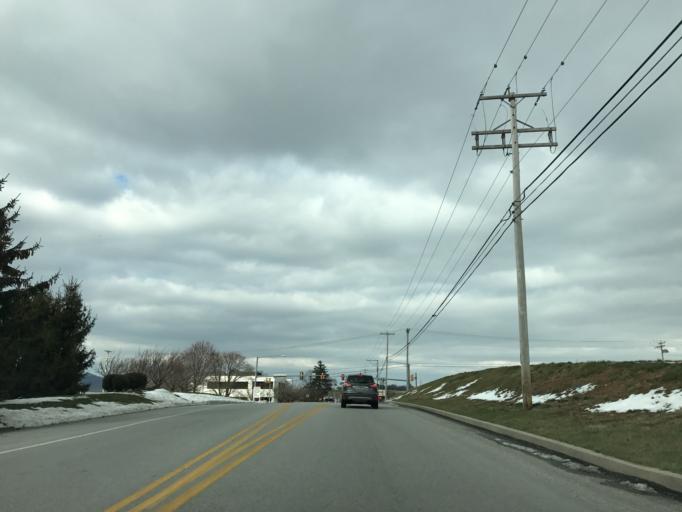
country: US
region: Pennsylvania
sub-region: York County
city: Parkville
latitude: 39.8074
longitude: -76.9477
